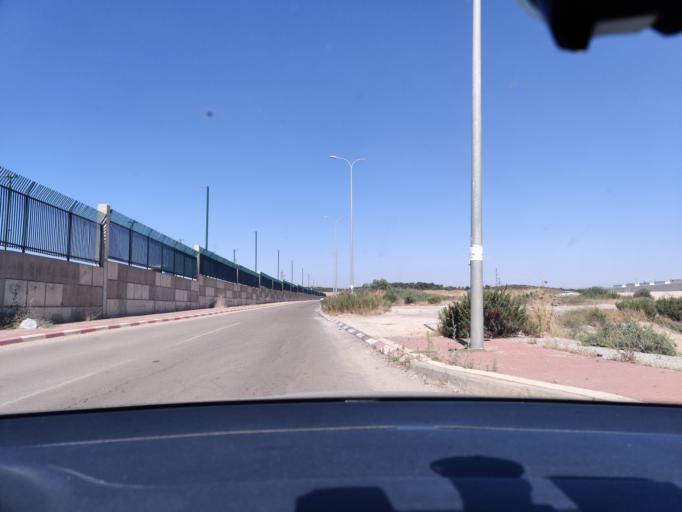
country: IL
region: Southern District
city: Qiryat Gat
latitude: 31.5912
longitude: 34.7883
